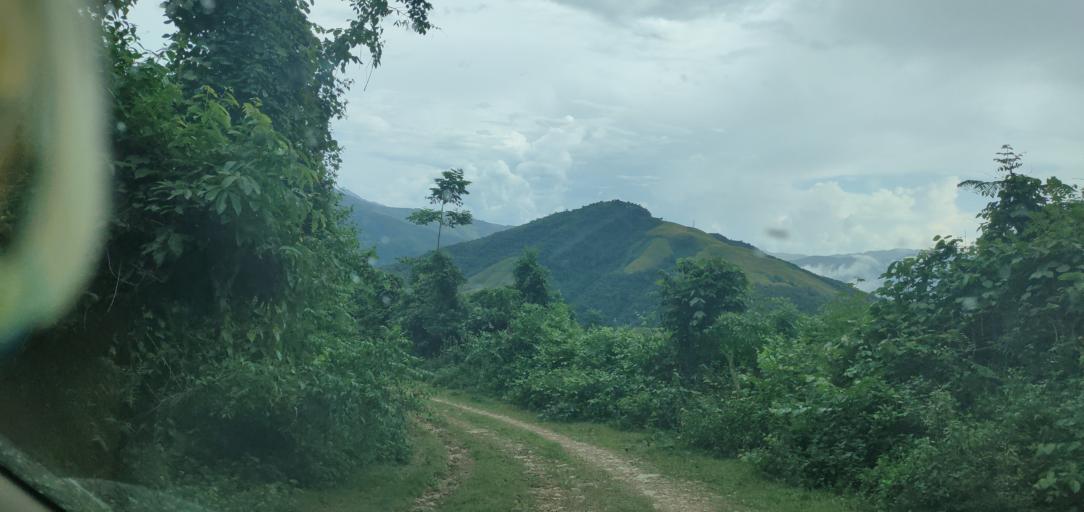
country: LA
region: Phongsali
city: Phongsali
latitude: 21.4400
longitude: 102.3282
